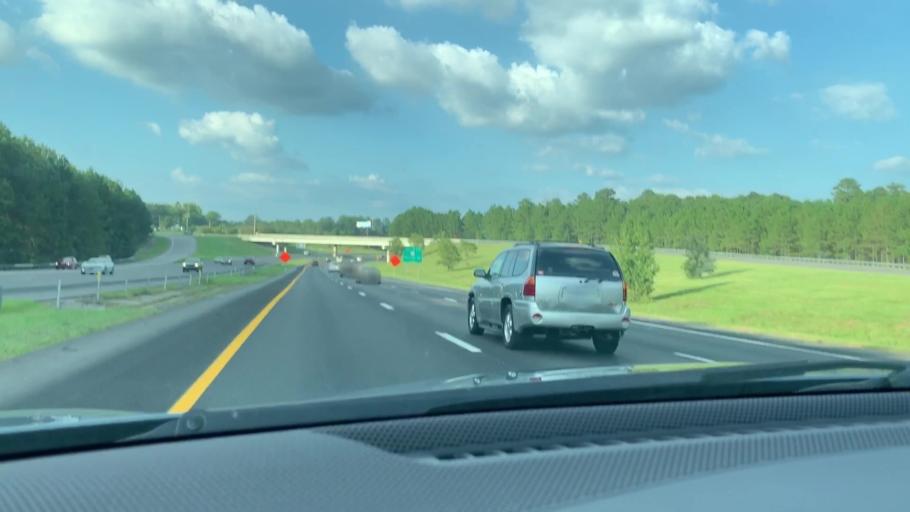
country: US
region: South Carolina
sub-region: Richland County
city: Woodfield
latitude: 34.0380
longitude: -80.9374
